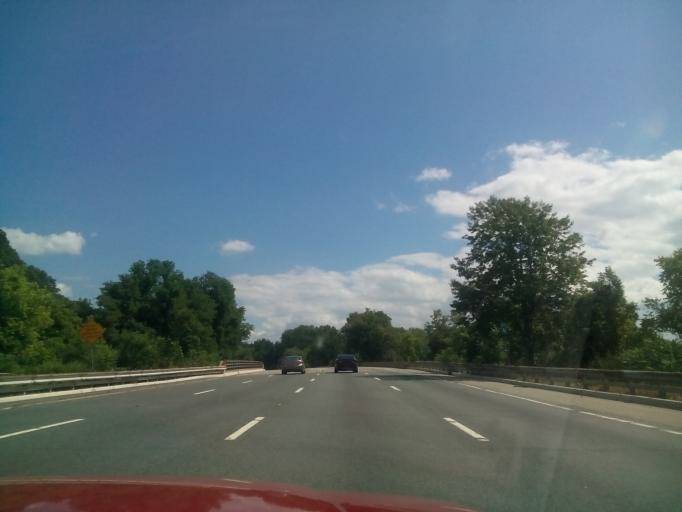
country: US
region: New Jersey
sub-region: Warren County
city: Belvidere
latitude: 40.9255
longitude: -75.0681
